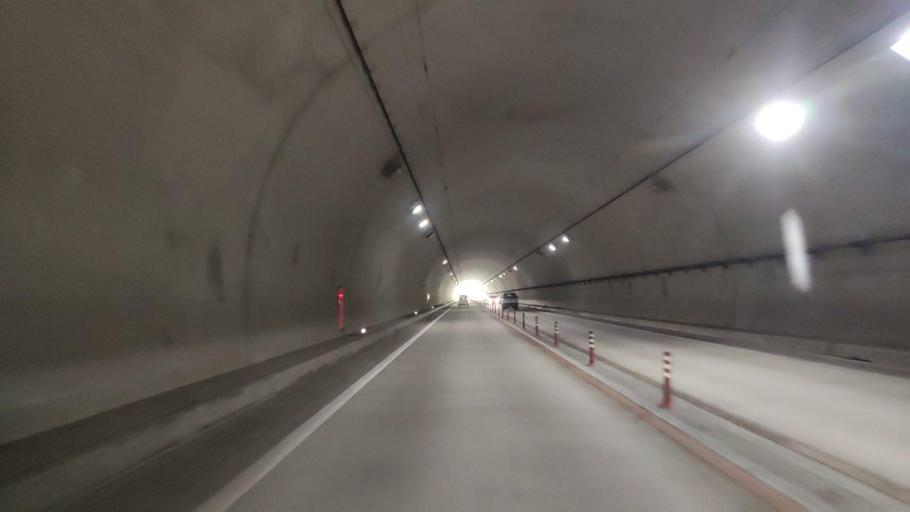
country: JP
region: Wakayama
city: Shingu
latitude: 33.6240
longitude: 135.9198
